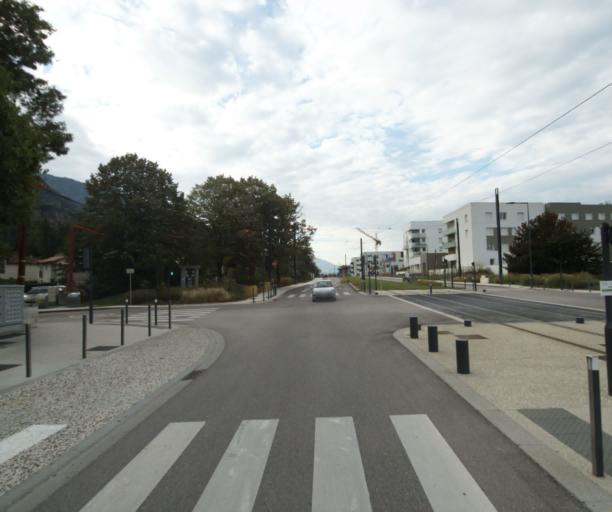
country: FR
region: Rhone-Alpes
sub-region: Departement de l'Isere
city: Fontanil-Cornillon
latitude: 45.2547
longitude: 5.6619
